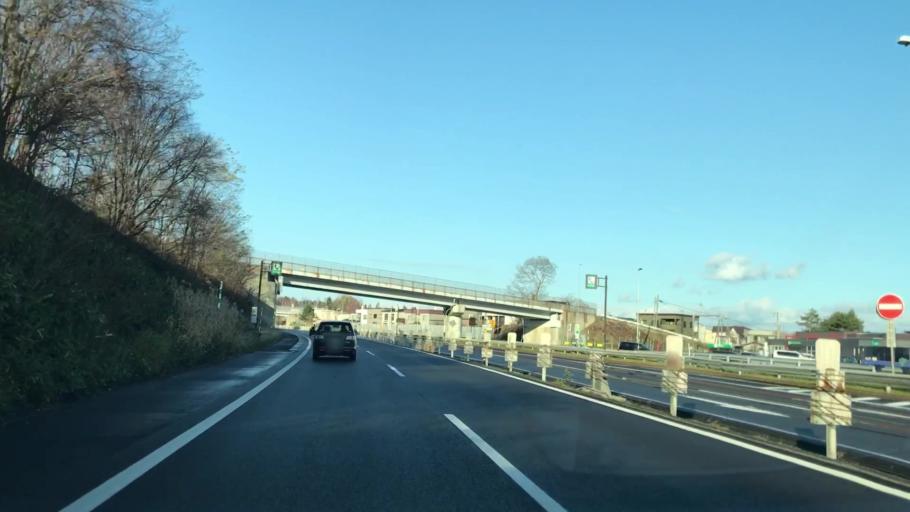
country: JP
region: Hokkaido
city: Sapporo
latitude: 43.1243
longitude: 141.2112
